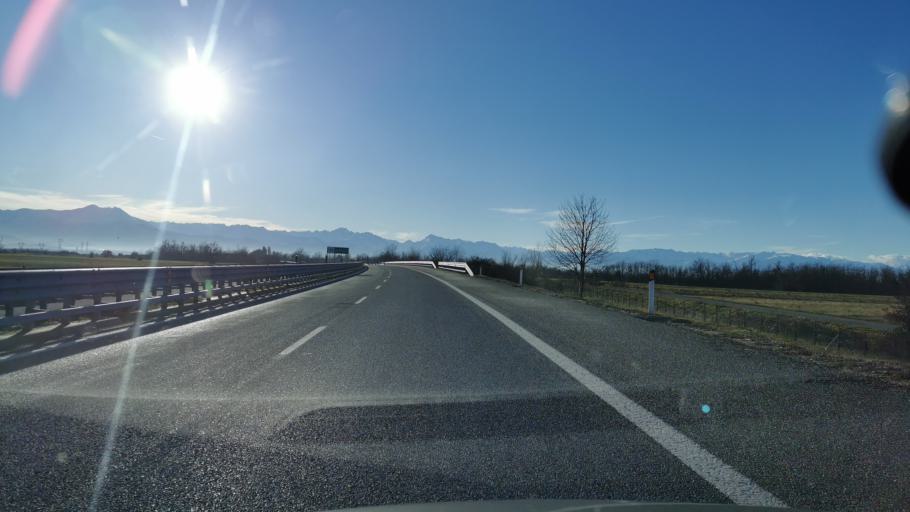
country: IT
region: Piedmont
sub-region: Provincia di Cuneo
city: Magliano Alpi
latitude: 44.4823
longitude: 7.7990
